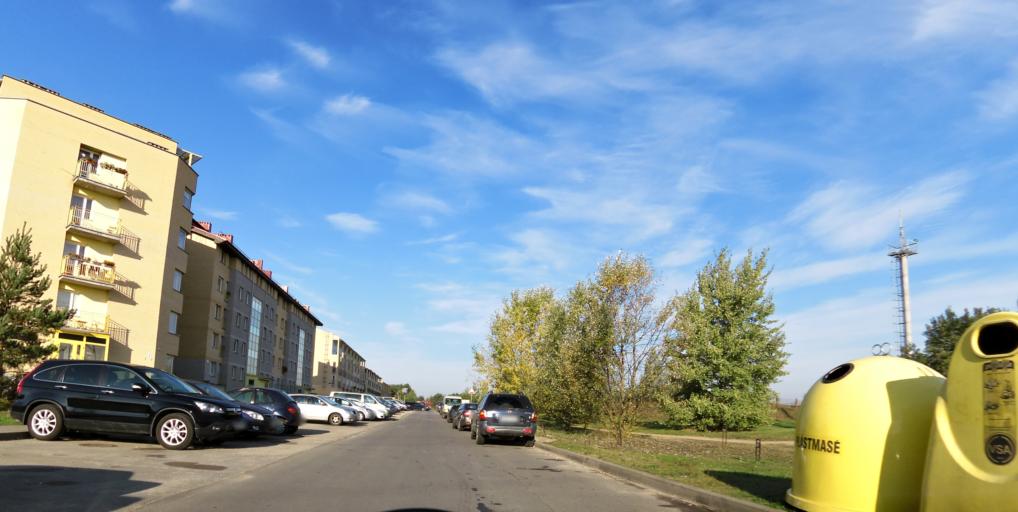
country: LT
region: Vilnius County
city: Pilaite
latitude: 54.7015
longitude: 25.1710
